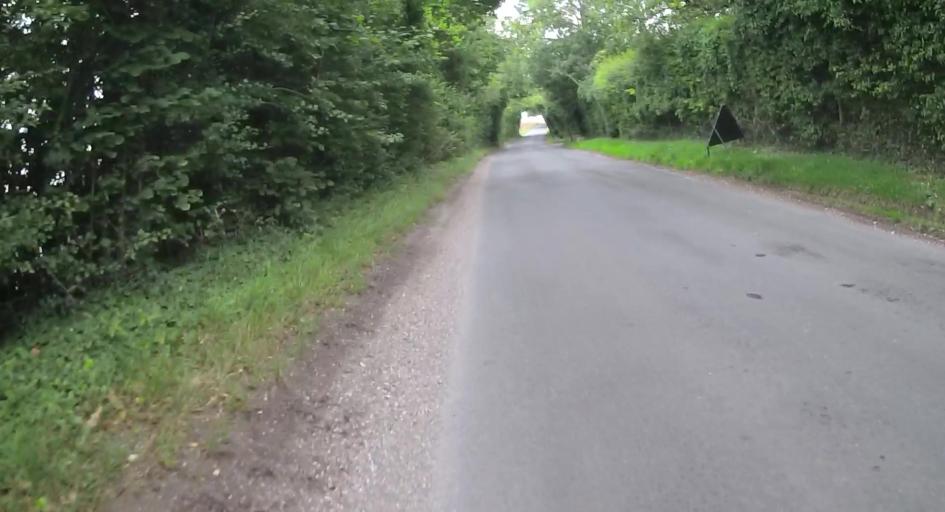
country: GB
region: England
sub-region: Hampshire
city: Bishops Waltham
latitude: 51.0272
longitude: -1.2049
